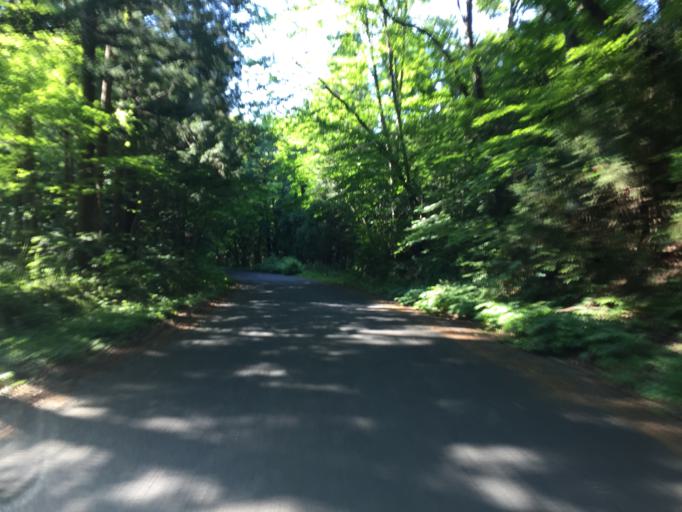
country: JP
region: Ibaraki
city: Kitaibaraki
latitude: 36.8745
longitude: 140.6687
